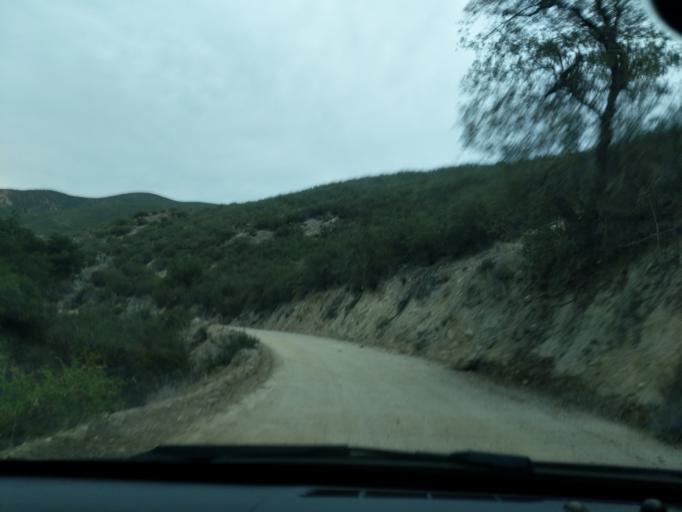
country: US
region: California
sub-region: Monterey County
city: Soledad
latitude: 36.5637
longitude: -121.2025
